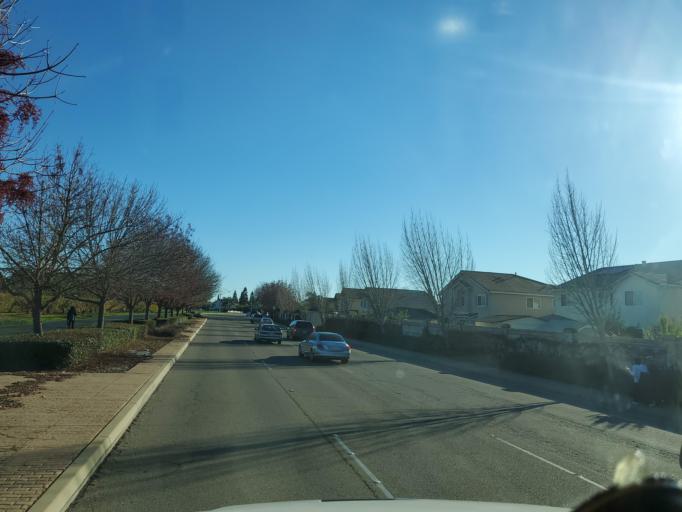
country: US
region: California
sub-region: San Joaquin County
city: August
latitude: 38.0082
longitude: -121.2725
